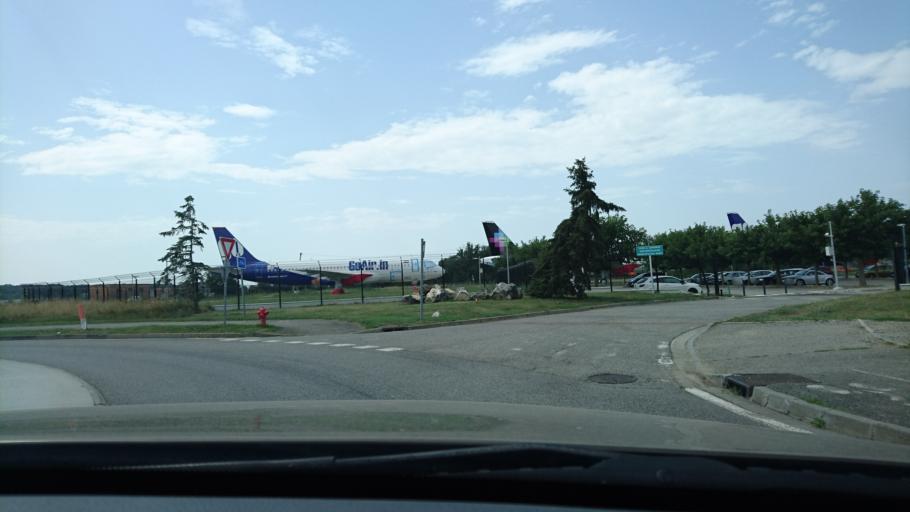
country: FR
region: Midi-Pyrenees
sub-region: Departement de la Haute-Garonne
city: Cornebarrieu
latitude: 43.6459
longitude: 1.3511
